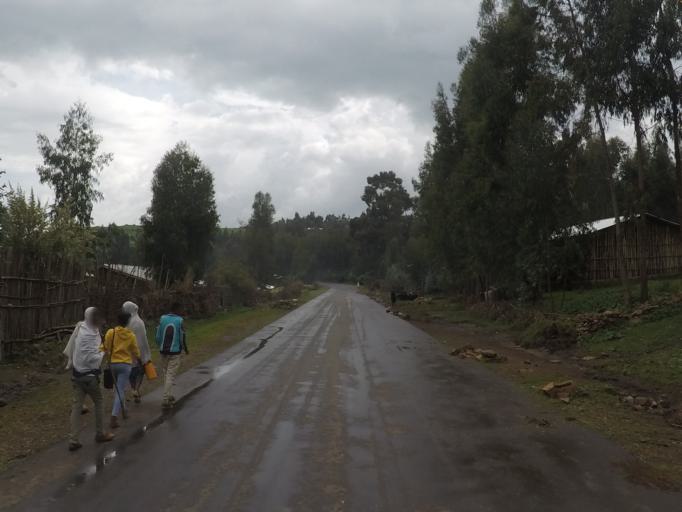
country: ET
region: Amhara
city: Dabat
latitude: 13.0605
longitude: 37.8226
